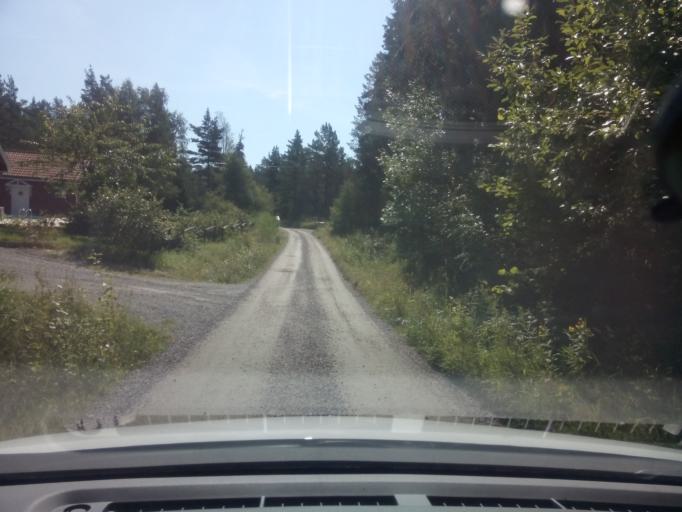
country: SE
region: Soedermanland
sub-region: Oxelosunds Kommun
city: Oxelosund
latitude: 58.7343
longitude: 17.2205
